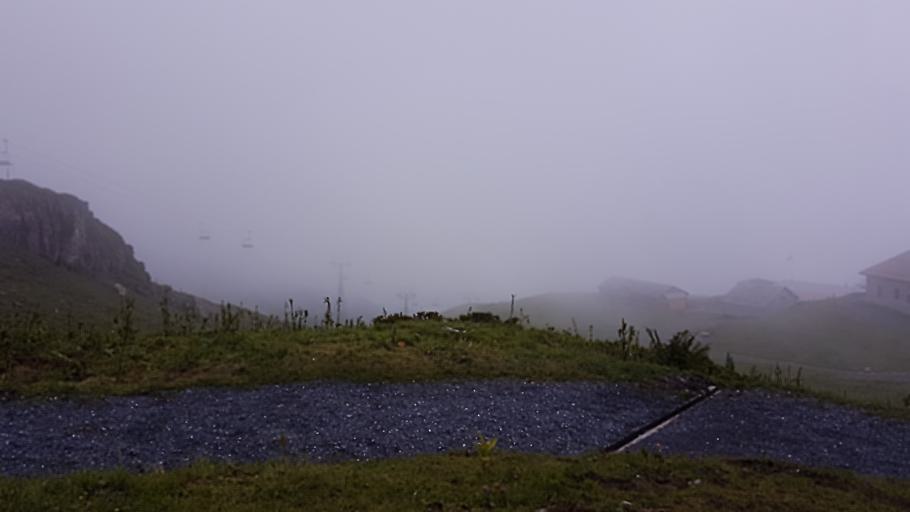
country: CH
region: Saint Gallen
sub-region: Wahlkreis Sarganserland
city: Sargans
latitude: 46.9908
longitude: 9.4132
